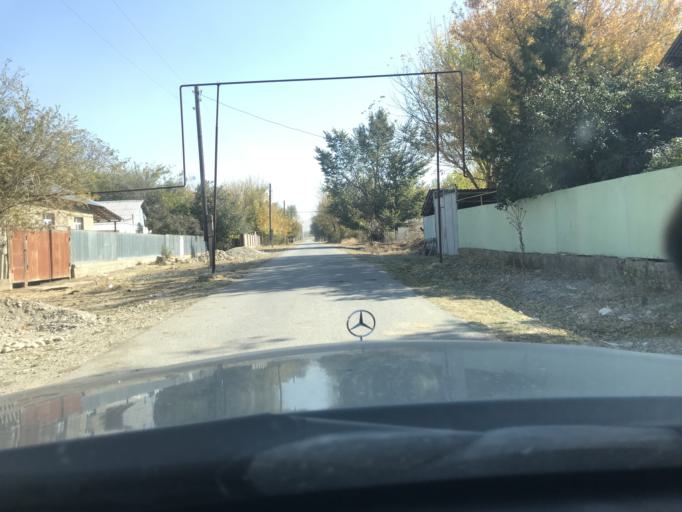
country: KZ
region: Ongtustik Qazaqstan
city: Sastobe
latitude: 42.5445
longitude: 69.9328
